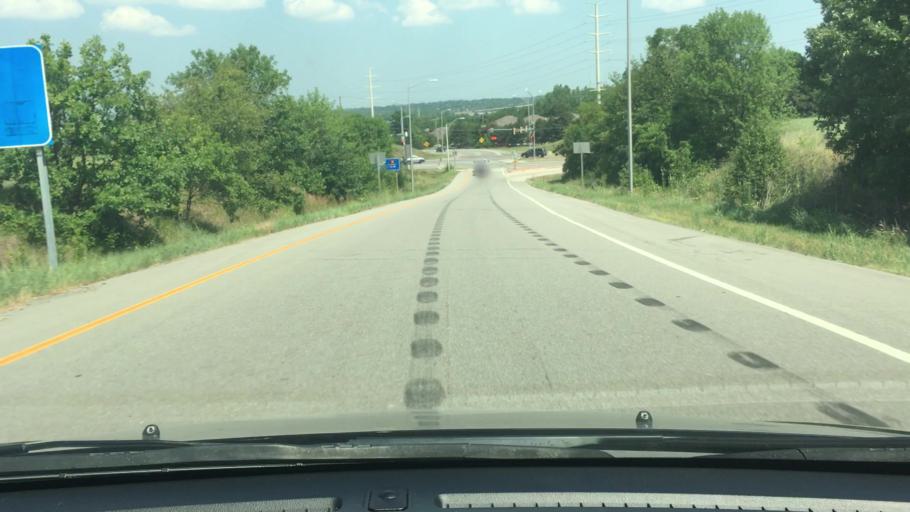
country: US
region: Kansas
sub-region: Johnson County
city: Lenexa
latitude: 38.9115
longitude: -94.6964
